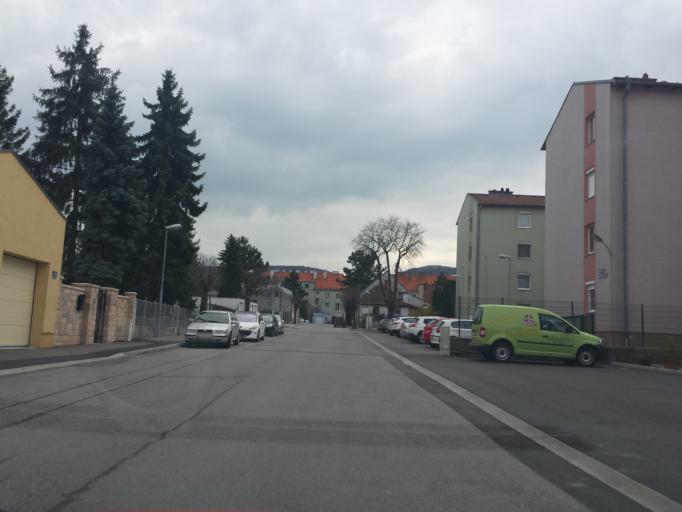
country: AT
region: Lower Austria
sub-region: Politischer Bezirk Bruck an der Leitha
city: Hainburg an der Donau
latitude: 48.1464
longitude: 16.9548
